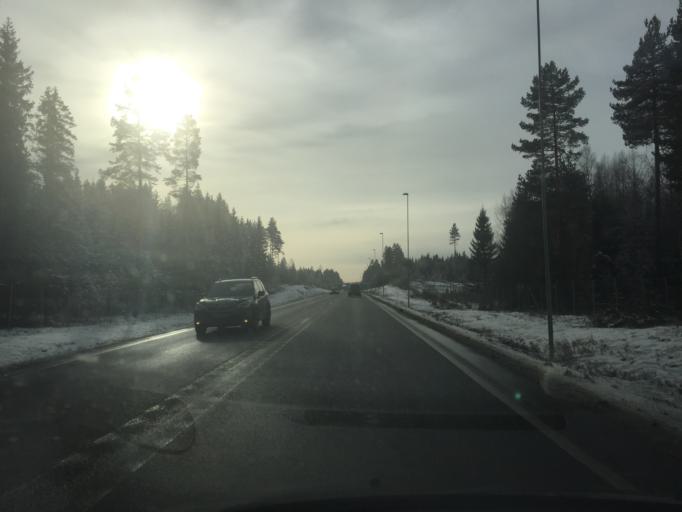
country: NO
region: Hedmark
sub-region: Loten
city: Loten
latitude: 60.7613
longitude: 11.3079
